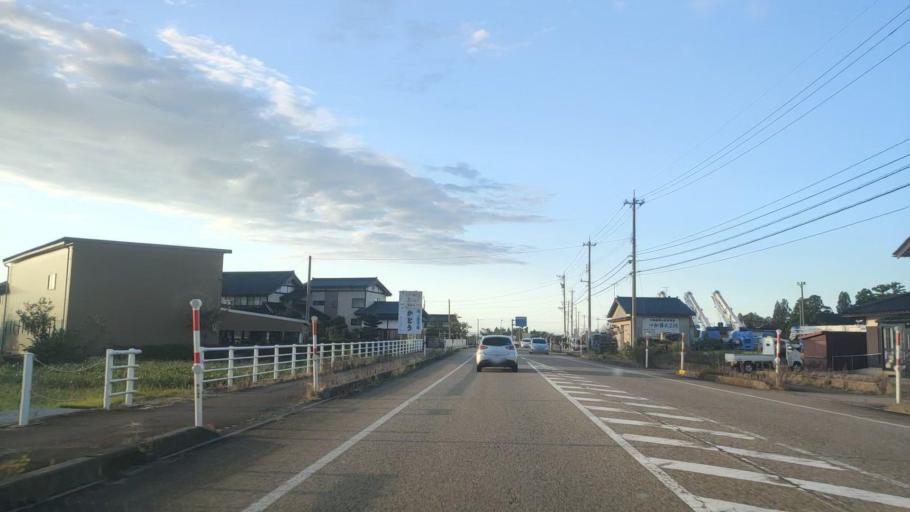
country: JP
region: Toyama
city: Nanto-shi
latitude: 36.5902
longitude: 136.9648
